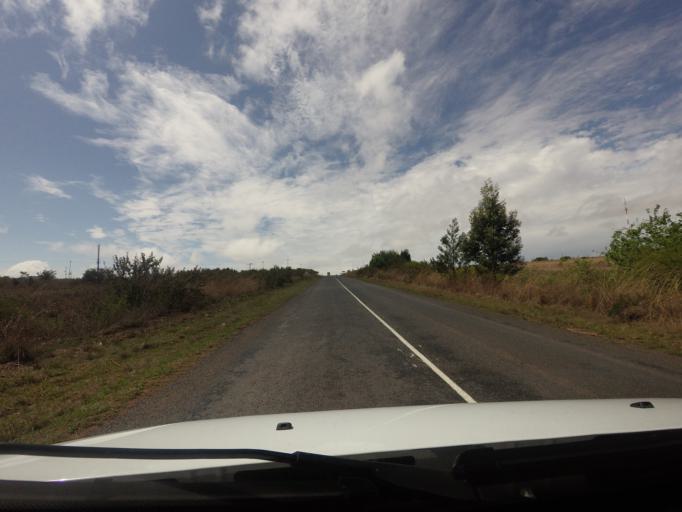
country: ZA
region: Mpumalanga
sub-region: Ehlanzeni District
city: Lydenburg
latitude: -25.1707
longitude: 30.3728
